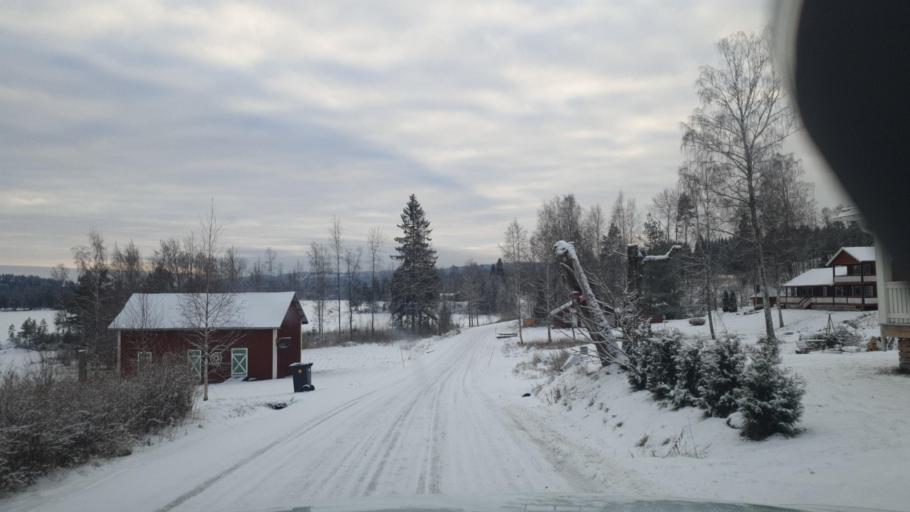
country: NO
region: Ostfold
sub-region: Romskog
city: Romskog
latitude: 59.8473
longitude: 11.9644
